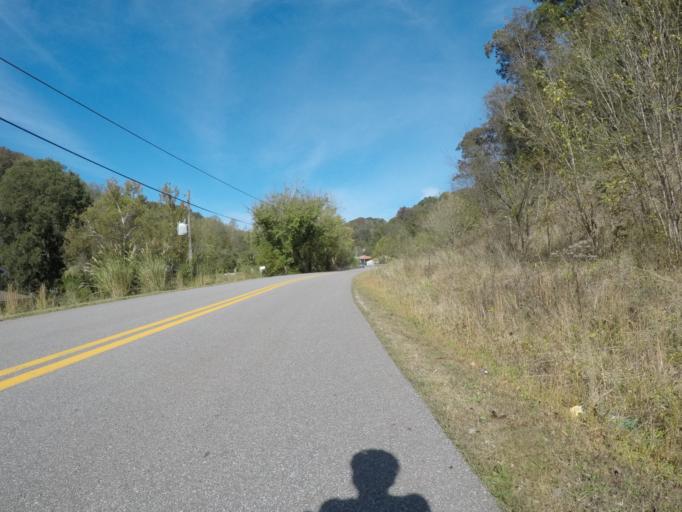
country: US
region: West Virginia
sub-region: Wayne County
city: Lavalette
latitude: 38.3460
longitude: -82.4503
